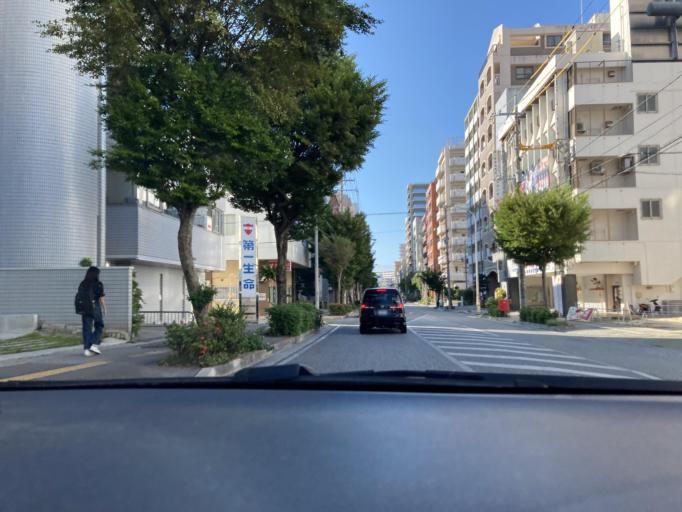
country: JP
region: Okinawa
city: Naha-shi
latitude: 26.2207
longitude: 127.6893
